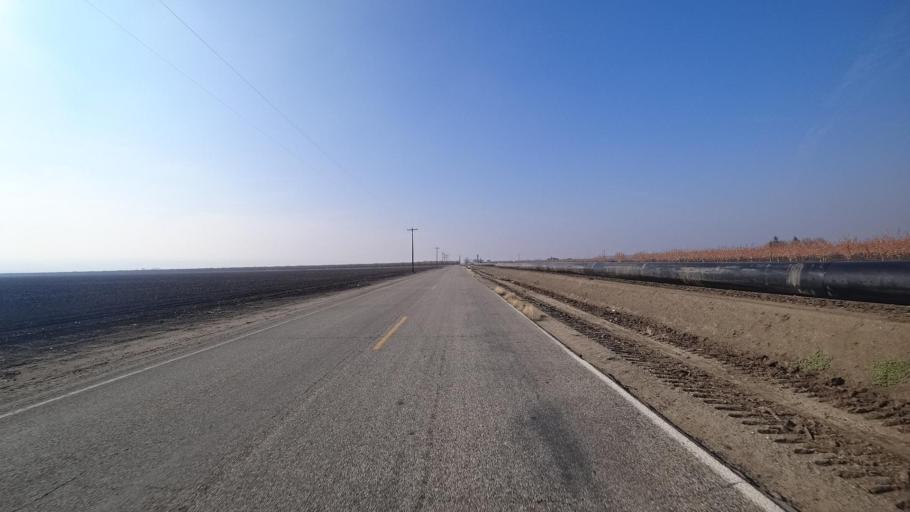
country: US
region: California
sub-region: Kern County
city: Buttonwillow
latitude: 35.3546
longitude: -119.4076
